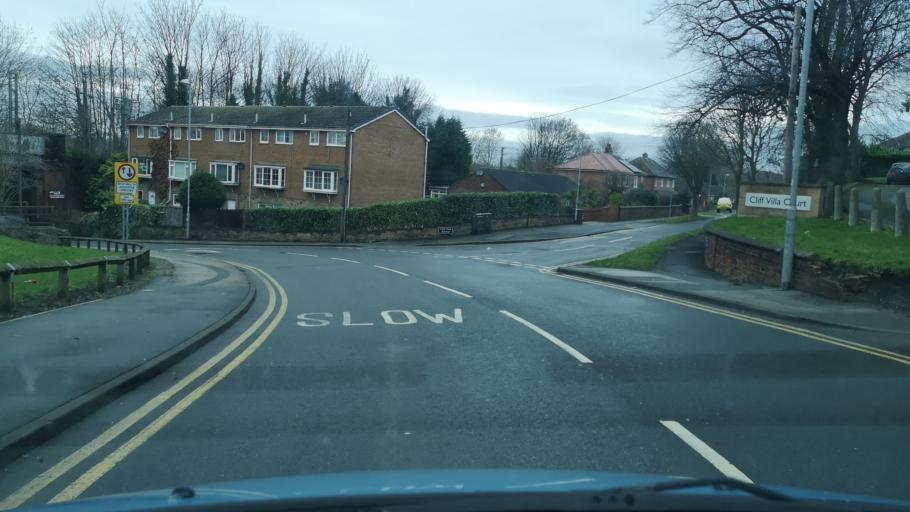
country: GB
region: England
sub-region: City and Borough of Wakefield
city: Wakefield
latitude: 53.6858
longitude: -1.5071
